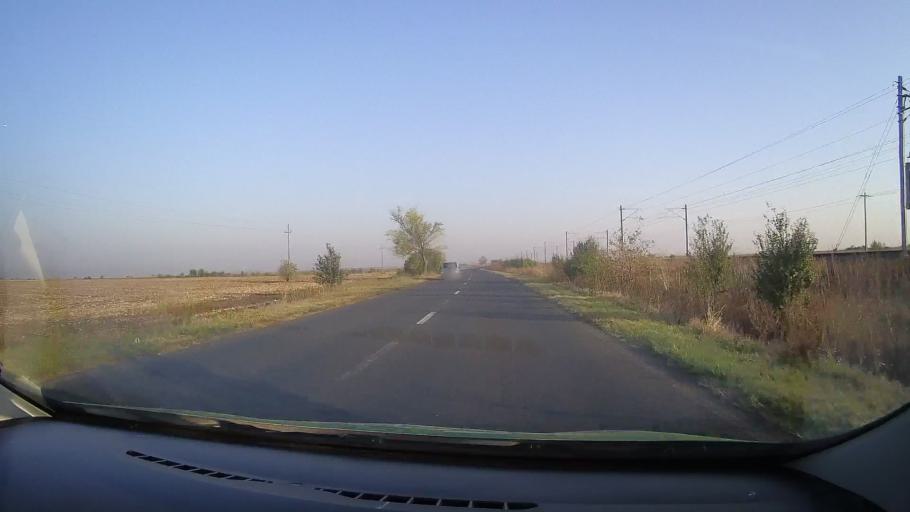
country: RO
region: Arad
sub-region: Comuna Sofronea
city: Sofronea
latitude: 46.2933
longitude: 21.3115
